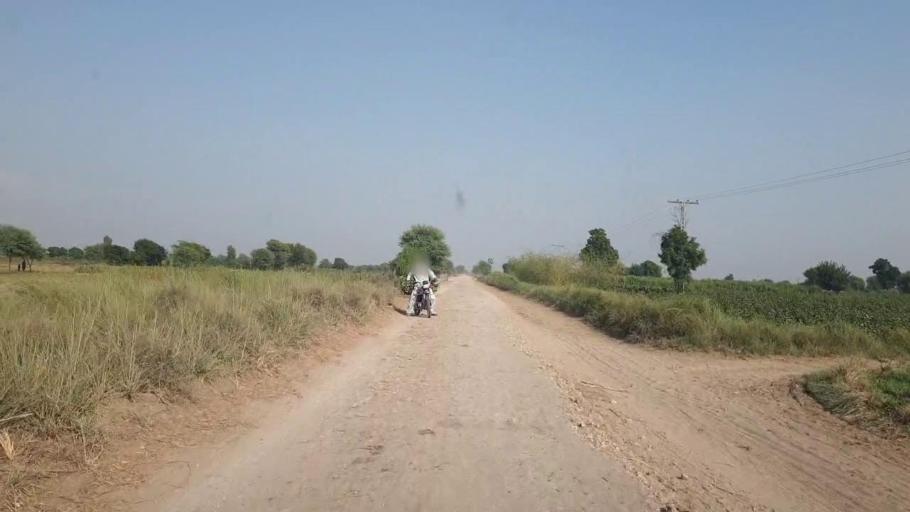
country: PK
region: Sindh
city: Sinjhoro
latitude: 26.0558
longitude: 68.8520
